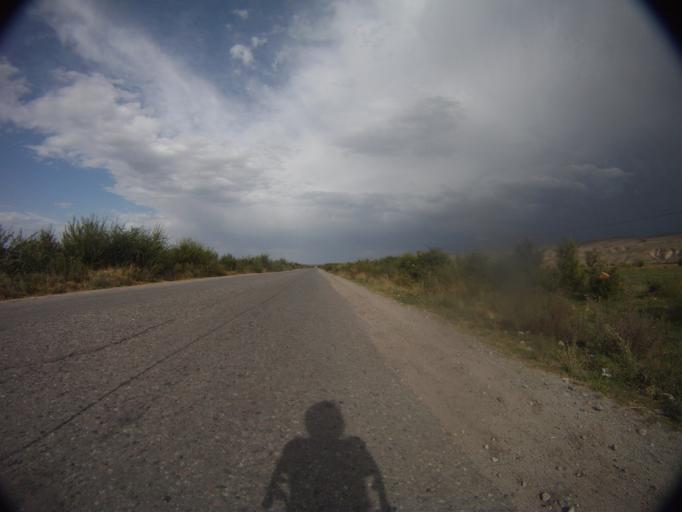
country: KG
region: Ysyk-Koel
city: Pokrovka
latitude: 42.2833
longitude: 77.7999
